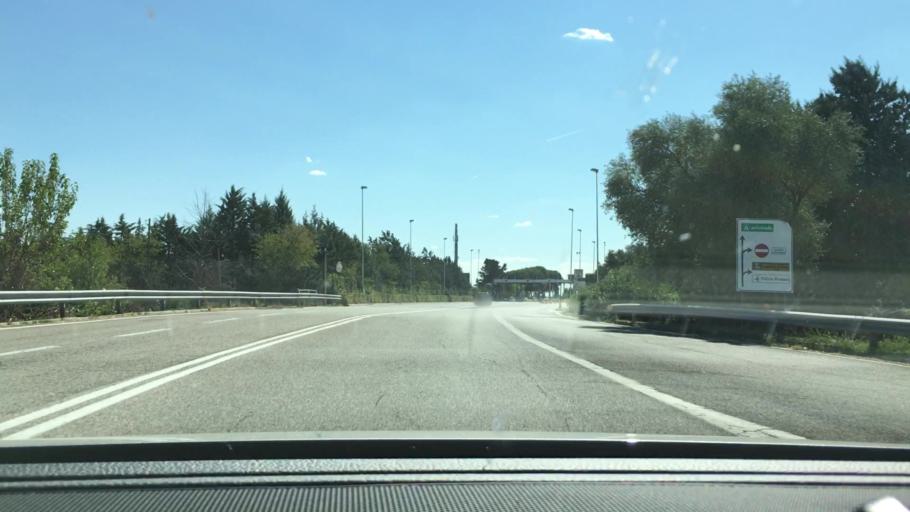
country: IT
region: Apulia
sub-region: Provincia di Bari
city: Bitritto
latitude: 41.0705
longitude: 16.8305
